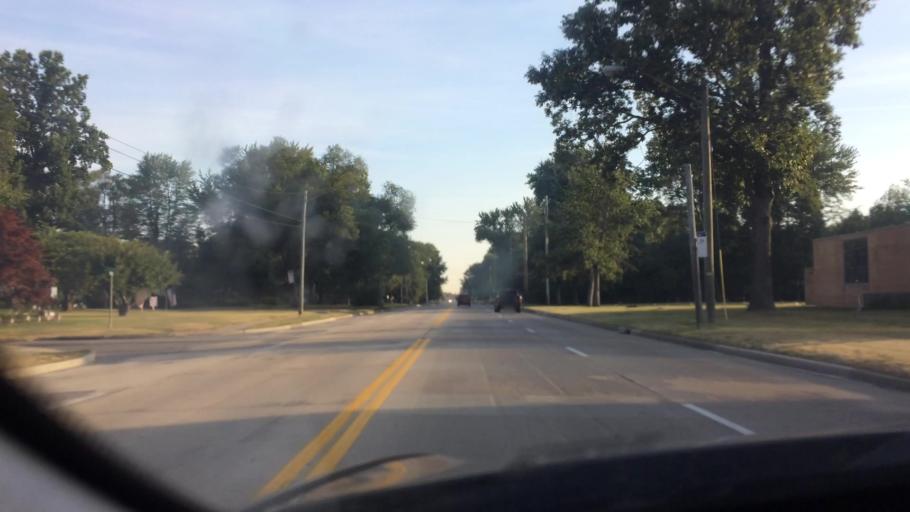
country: US
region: Ohio
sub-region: Lucas County
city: Ottawa Hills
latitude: 41.6818
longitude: -83.6442
